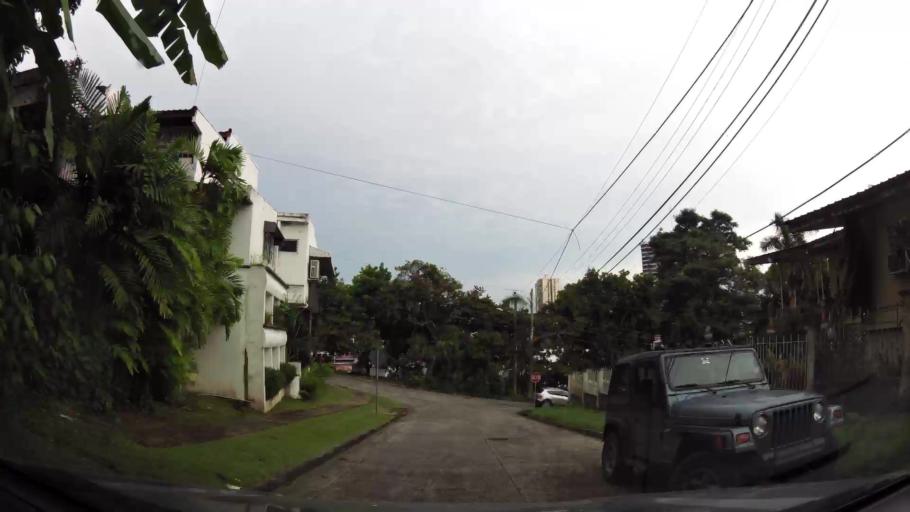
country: PA
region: Panama
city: Panama
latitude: 9.0162
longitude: -79.5238
